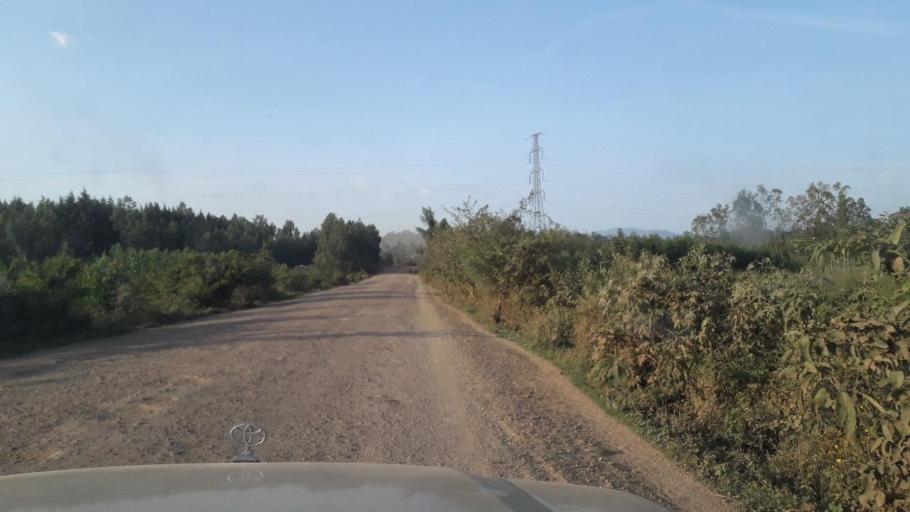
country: ET
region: Oromiya
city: Jima
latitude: 7.6162
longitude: 36.8340
